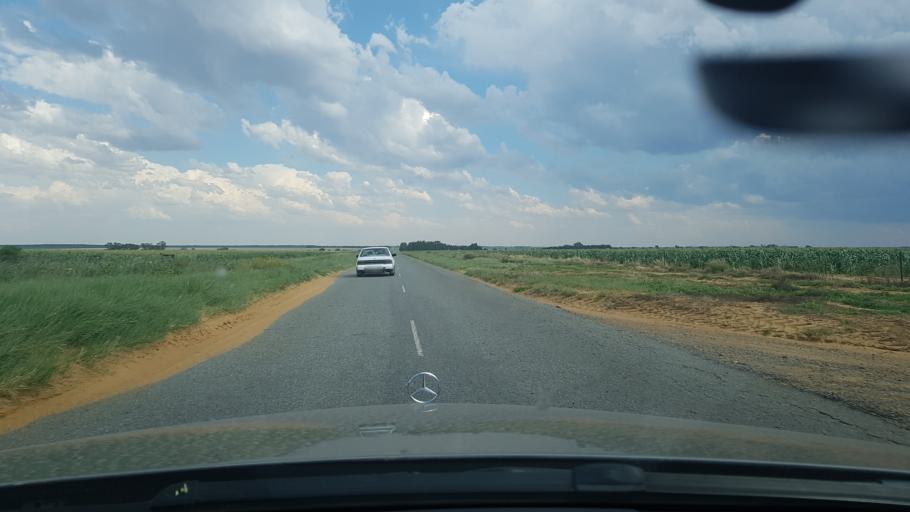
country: ZA
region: North-West
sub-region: Dr Ruth Segomotsi Mompati District Municipality
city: Bloemhof
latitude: -27.8413
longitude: 25.6422
